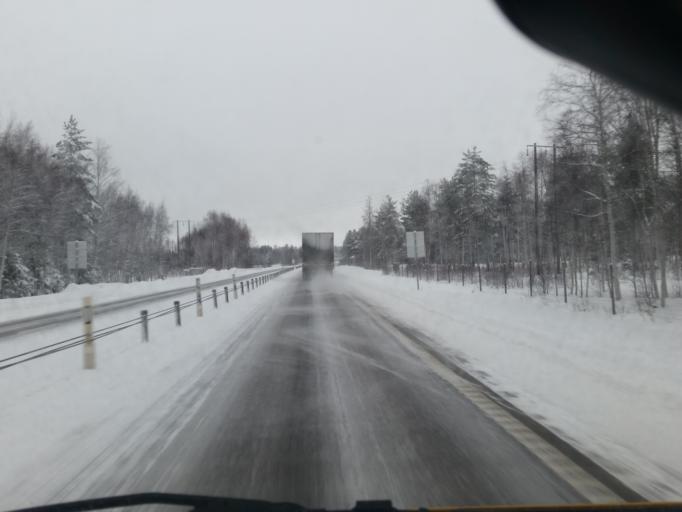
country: SE
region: Norrbotten
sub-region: Pitea Kommun
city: Bergsviken
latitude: 65.2934
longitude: 21.4267
